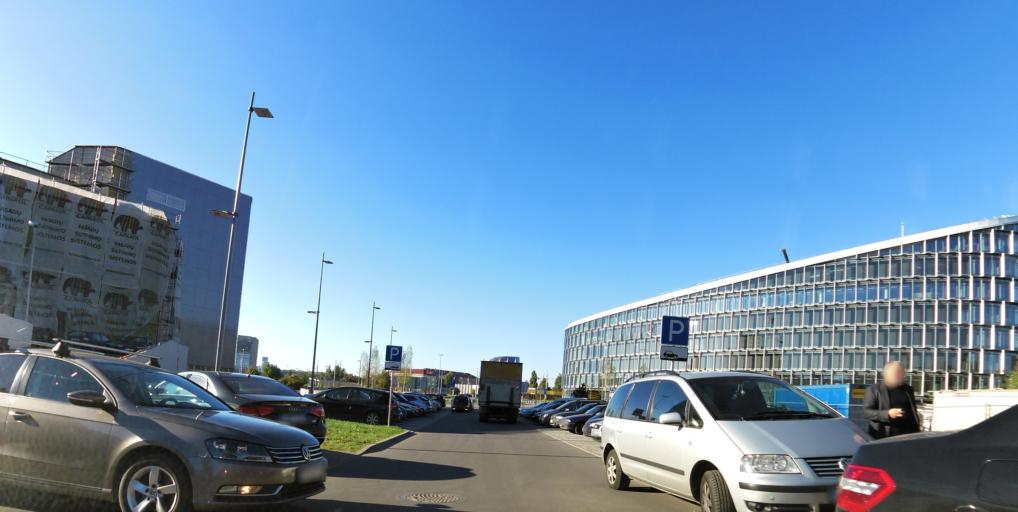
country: LT
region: Vilnius County
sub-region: Vilnius
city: Vilnius
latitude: 54.7002
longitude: 25.2669
